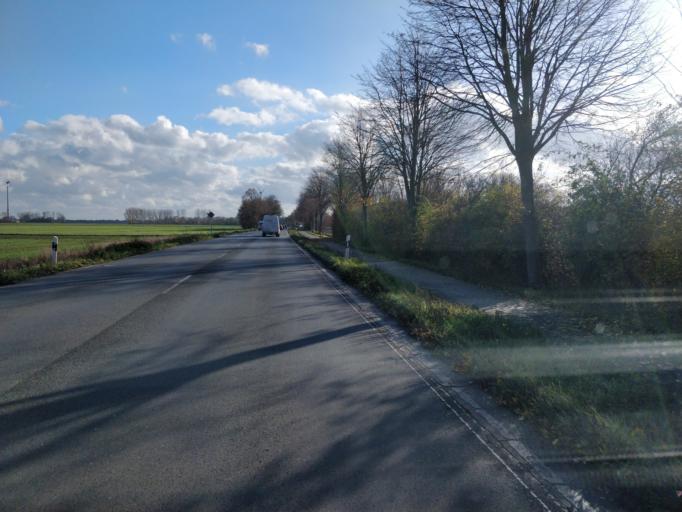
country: DE
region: North Rhine-Westphalia
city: Rees
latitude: 51.7924
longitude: 6.3730
